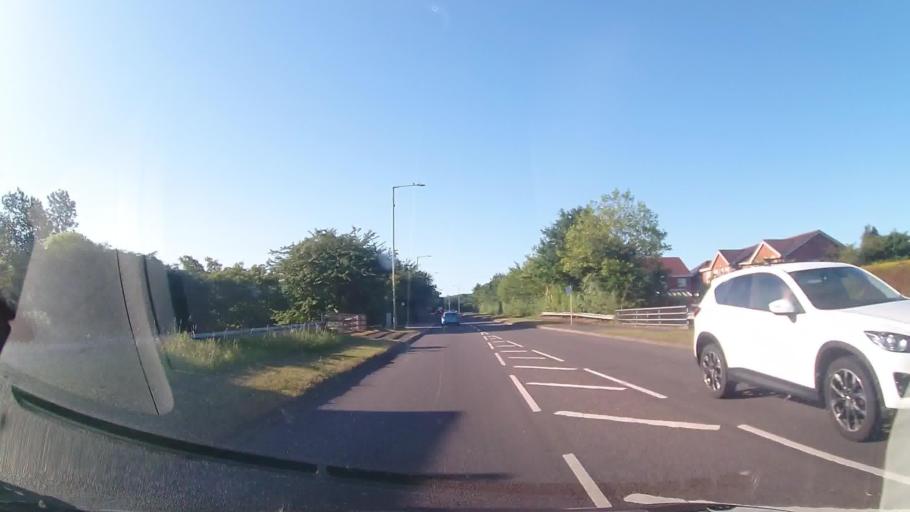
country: GB
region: England
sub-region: Telford and Wrekin
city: Eyton upon the Weald Moors
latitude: 52.7193
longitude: -2.5343
